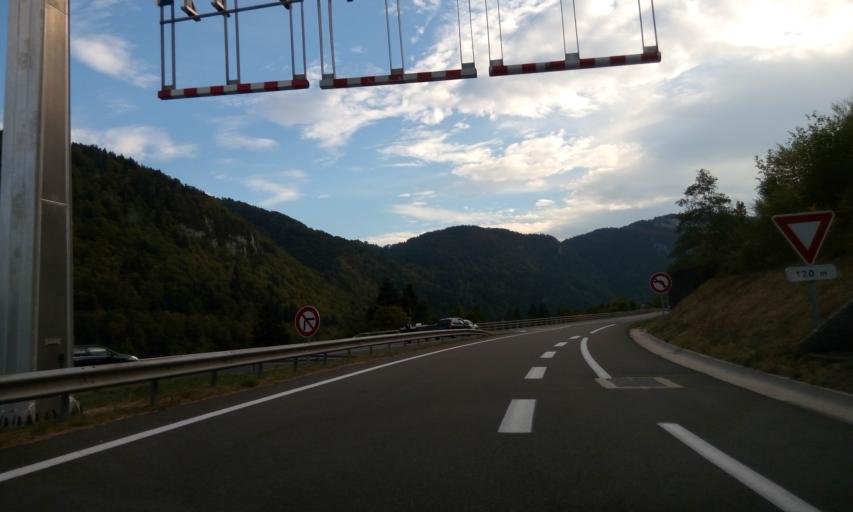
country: FR
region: Rhone-Alpes
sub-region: Departement de l'Ain
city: Nantua
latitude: 46.1552
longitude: 5.6460
